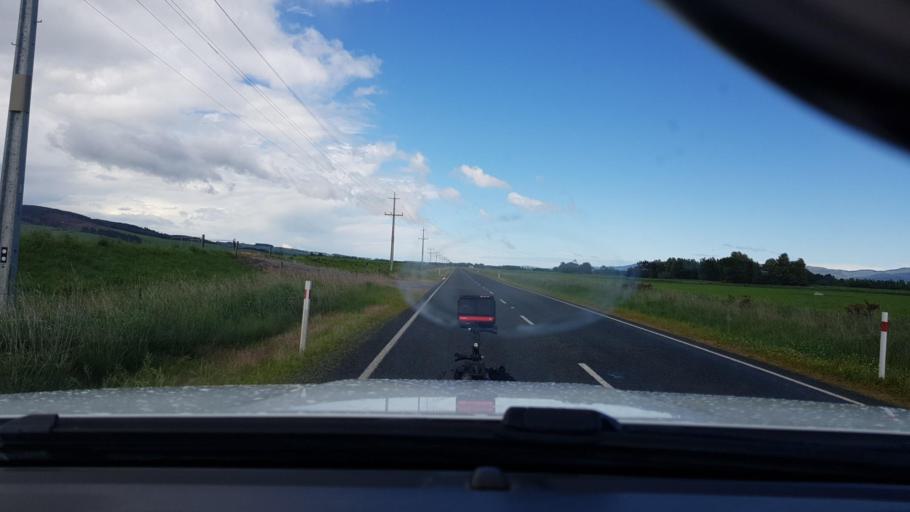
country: NZ
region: Southland
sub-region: Southland District
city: Winton
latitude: -45.8175
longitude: 168.3763
